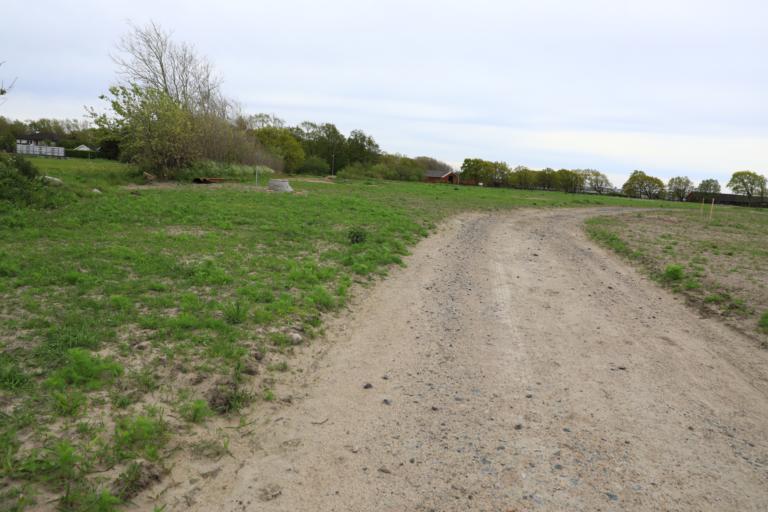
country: SE
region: Halland
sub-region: Varbergs Kommun
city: Varberg
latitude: 57.1463
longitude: 12.2378
